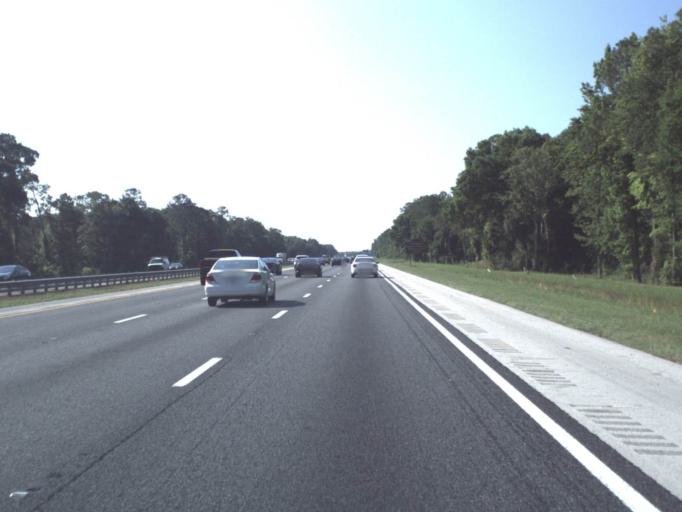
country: US
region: Florida
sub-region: Saint Johns County
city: Saint Augustine
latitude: 29.9430
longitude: -81.4325
